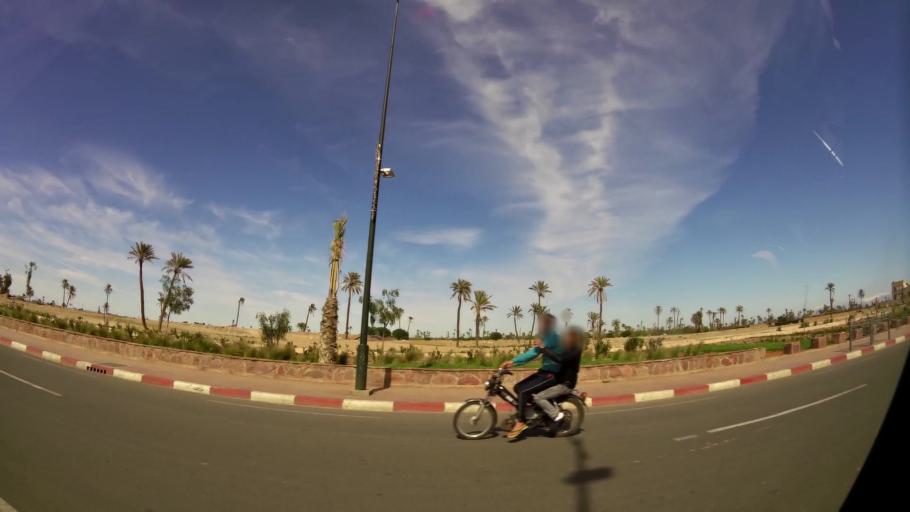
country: MA
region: Marrakech-Tensift-Al Haouz
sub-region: Marrakech
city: Marrakesh
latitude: 31.6309
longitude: -7.9734
